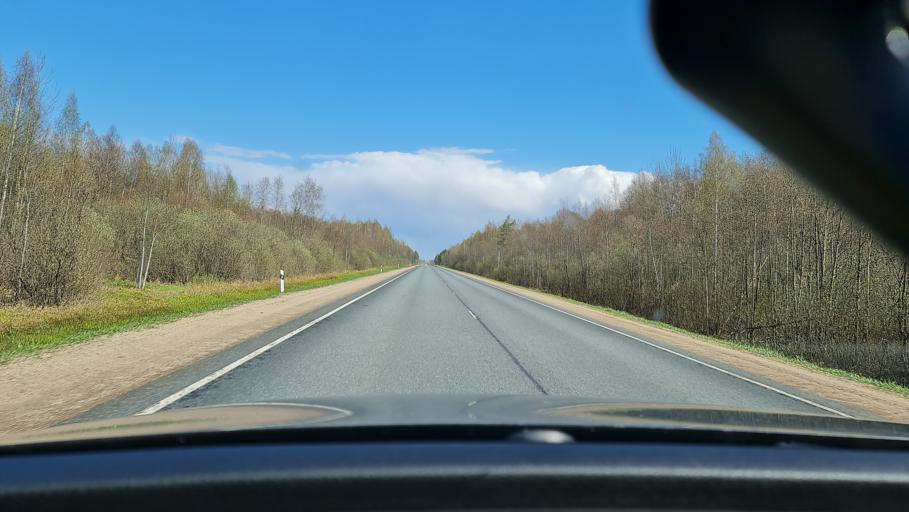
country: RU
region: Tverskaya
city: Rzhev
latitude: 56.2129
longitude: 34.1462
